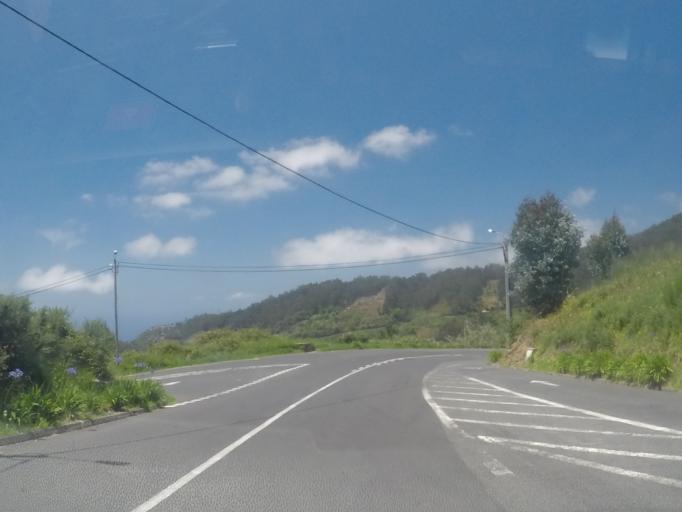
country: PT
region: Madeira
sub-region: Camara de Lobos
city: Curral das Freiras
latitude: 32.6853
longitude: -16.9865
